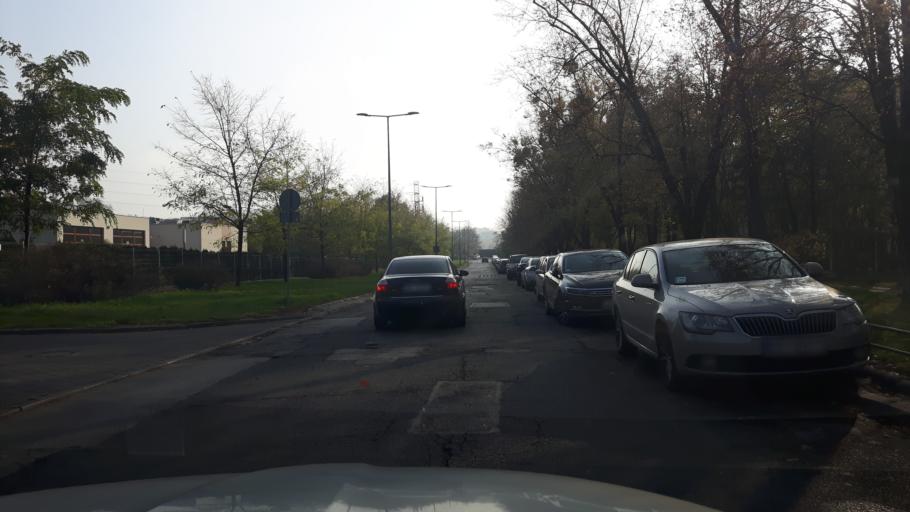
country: PL
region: Masovian Voivodeship
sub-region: Warszawa
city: Ochota
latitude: 52.1909
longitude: 20.9955
